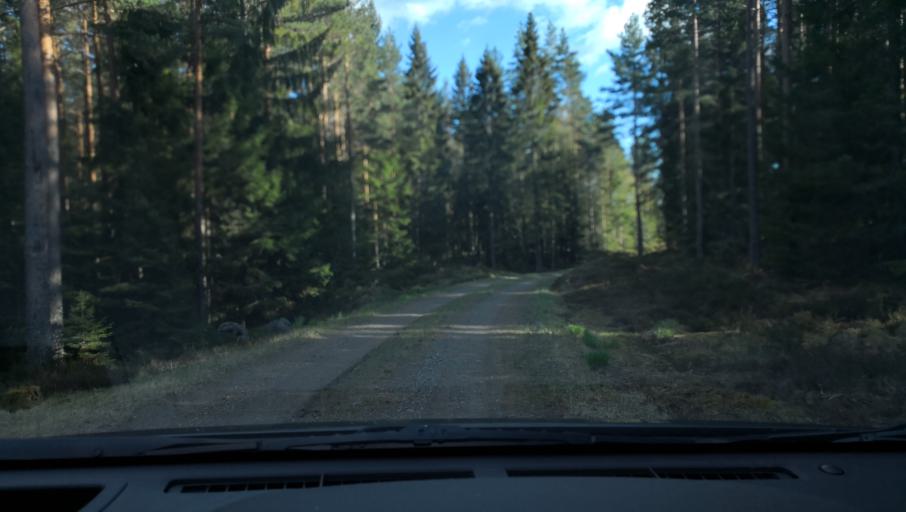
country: SE
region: OErebro
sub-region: Askersunds Kommun
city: Asbro
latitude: 58.8741
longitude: 15.1251
